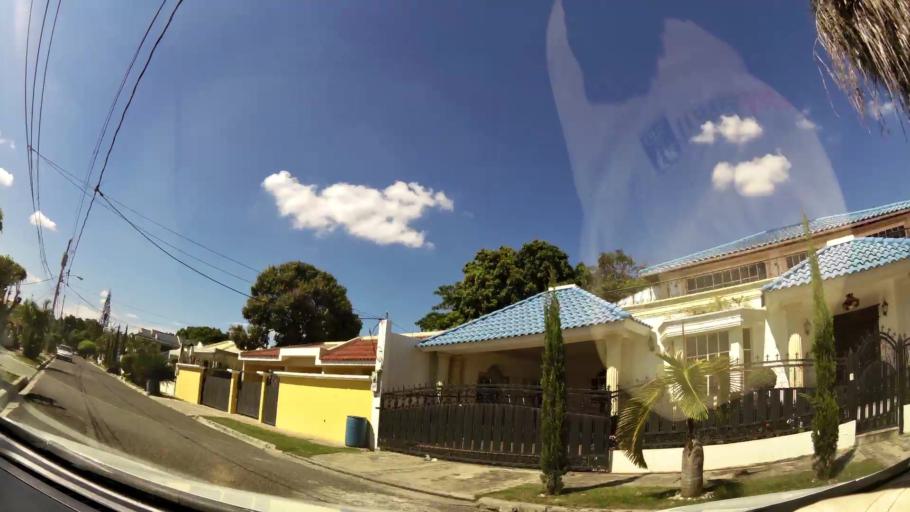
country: DO
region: Santiago
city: Santiago de los Caballeros
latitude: 19.4438
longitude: -70.6913
